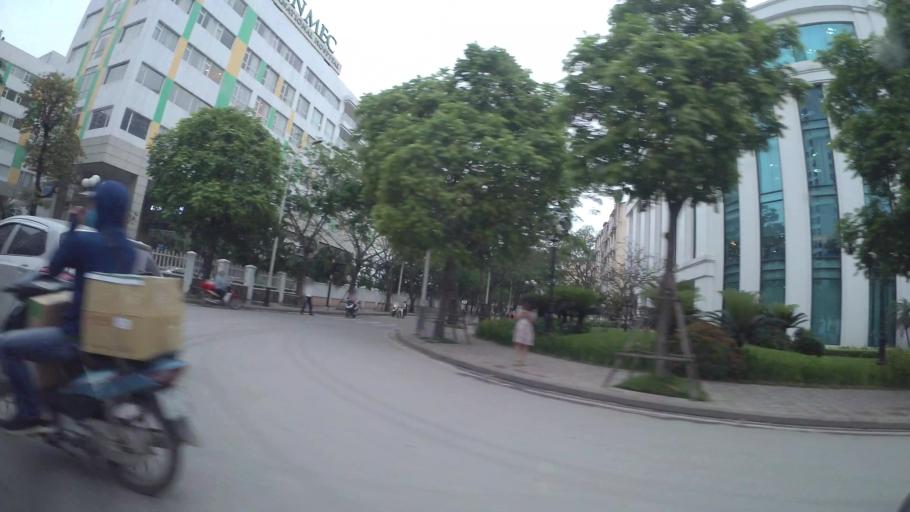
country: VN
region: Ha Noi
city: Hai BaTrung
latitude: 20.9969
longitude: 105.8675
